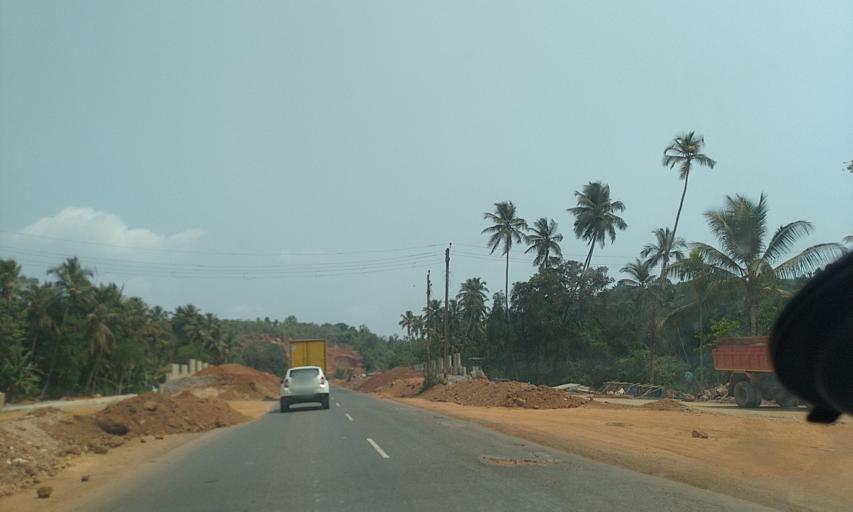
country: IN
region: Goa
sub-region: North Goa
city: Pernem
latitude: 15.7014
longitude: 73.8212
